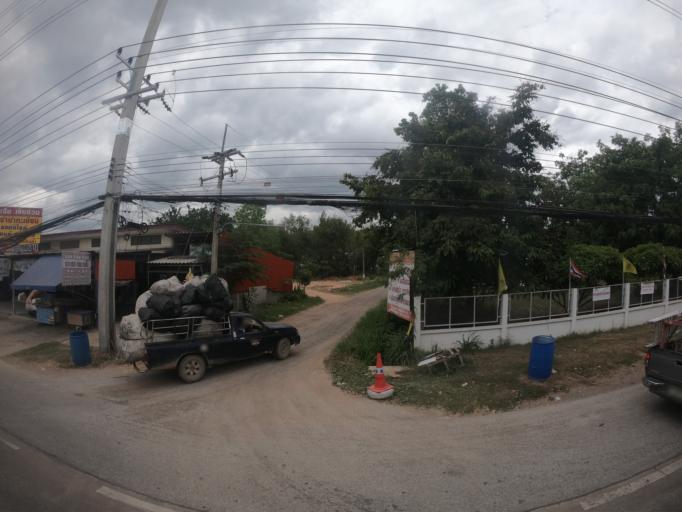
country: TH
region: Nakhon Ratchasima
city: Nakhon Ratchasima
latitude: 14.9177
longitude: 102.1475
